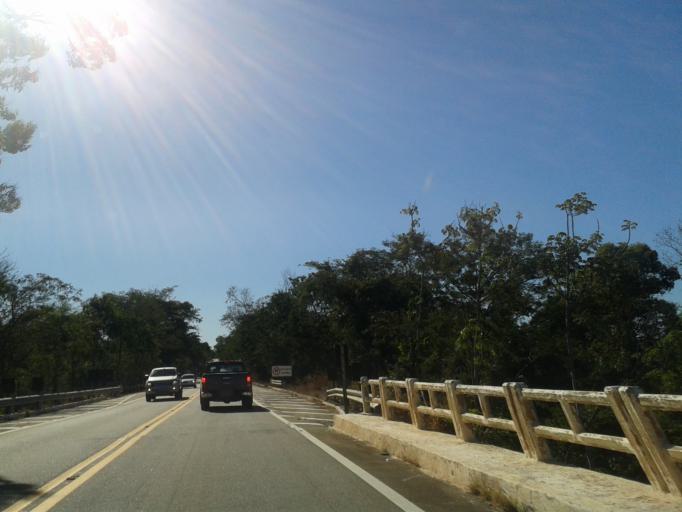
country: BR
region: Goias
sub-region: Itapuranga
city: Itapuranga
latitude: -15.5999
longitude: -50.2545
